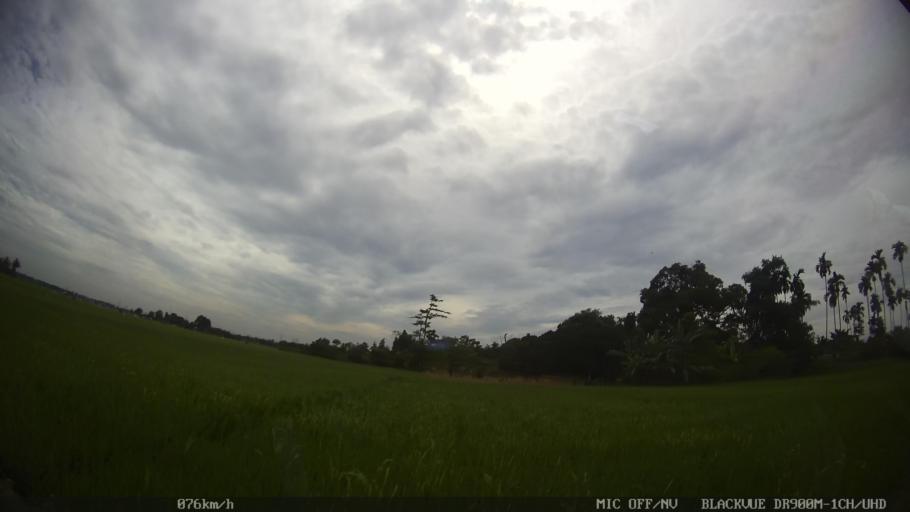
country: ID
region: North Sumatra
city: Sunggal
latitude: 3.5762
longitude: 98.5772
